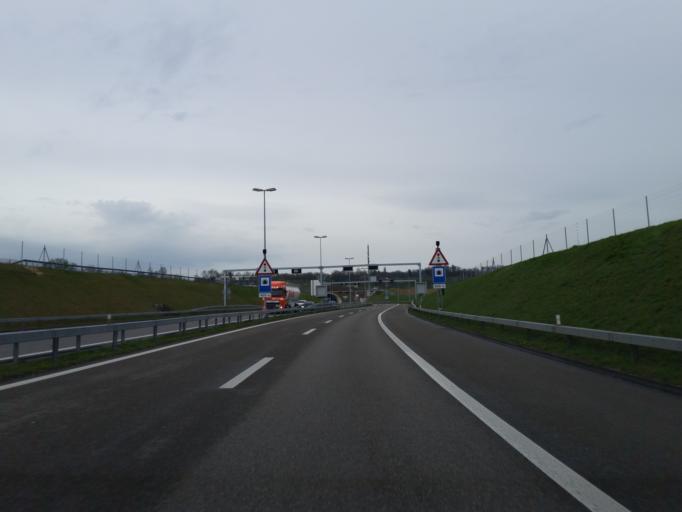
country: DE
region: Baden-Wuerttemberg
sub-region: Freiburg Region
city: Konstanz
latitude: 47.6538
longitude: 9.1574
